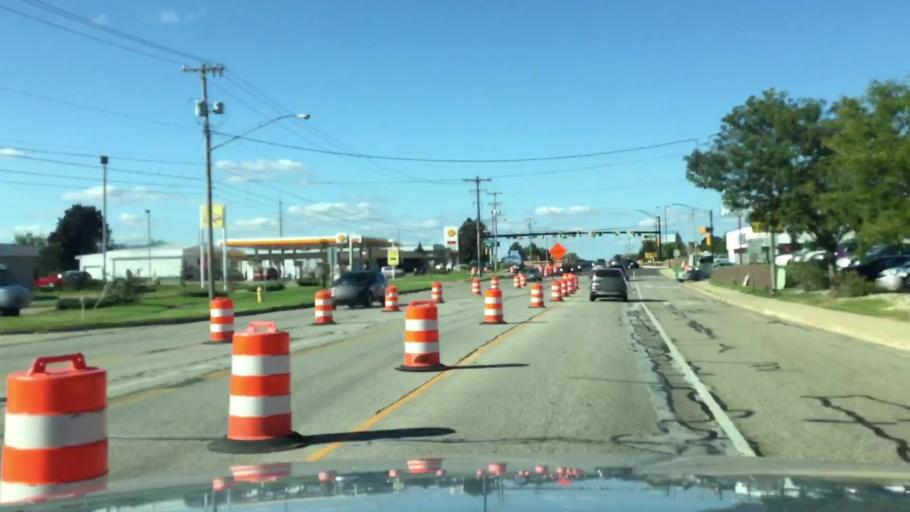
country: US
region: Michigan
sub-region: Kalamazoo County
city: Portage
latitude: 42.2140
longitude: -85.5894
